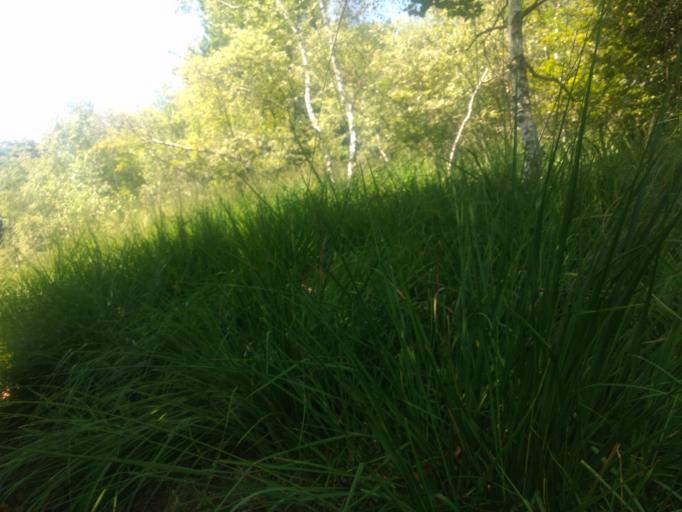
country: IT
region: Piedmont
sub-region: Provincia Verbano-Cusio-Ossola
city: Gabbio-Cereda-Ramate
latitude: 45.8922
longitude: 8.4524
